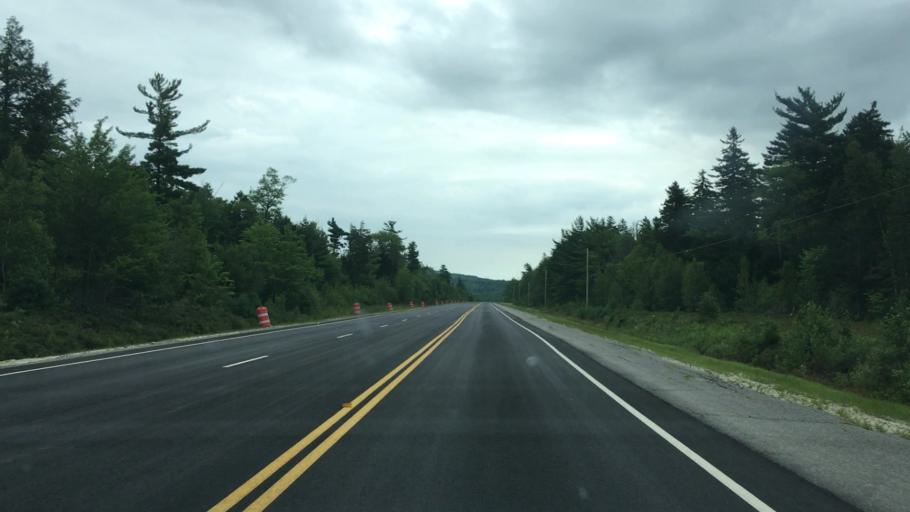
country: US
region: Maine
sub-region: Washington County
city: Cherryfield
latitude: 44.8758
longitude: -67.8913
